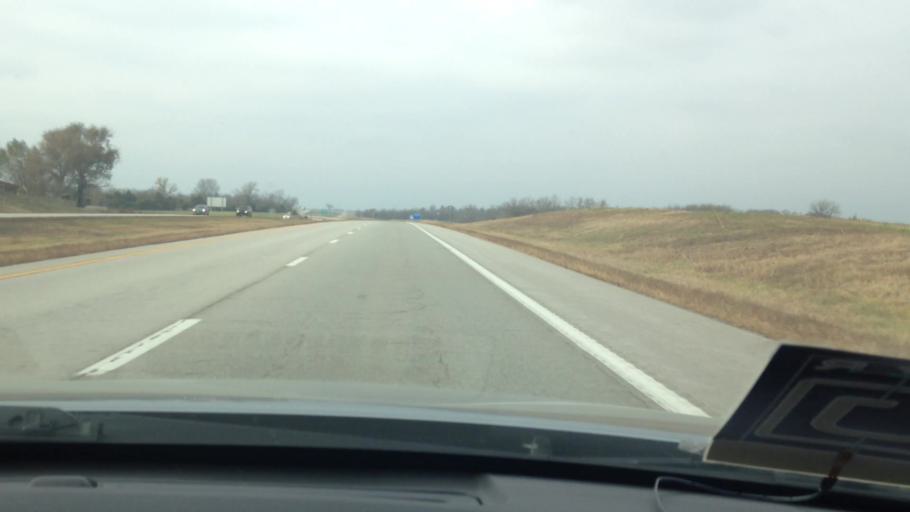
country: US
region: Missouri
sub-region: Cass County
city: Garden City
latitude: 38.5623
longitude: -94.1834
